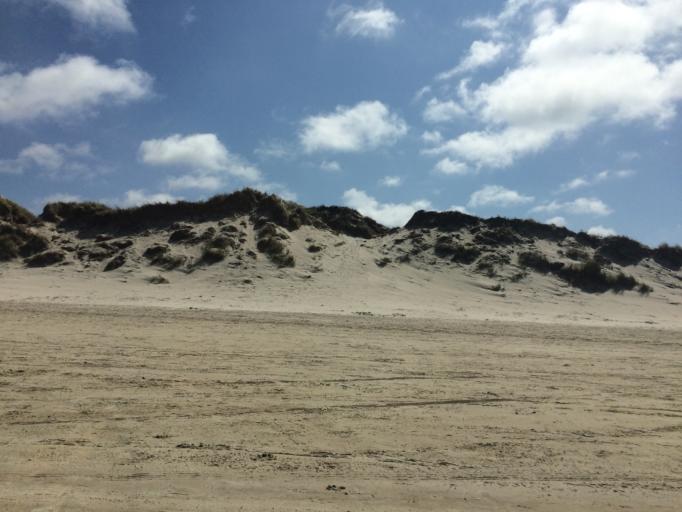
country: DK
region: North Denmark
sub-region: Jammerbugt Kommune
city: Pandrup
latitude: 57.2501
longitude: 9.5730
